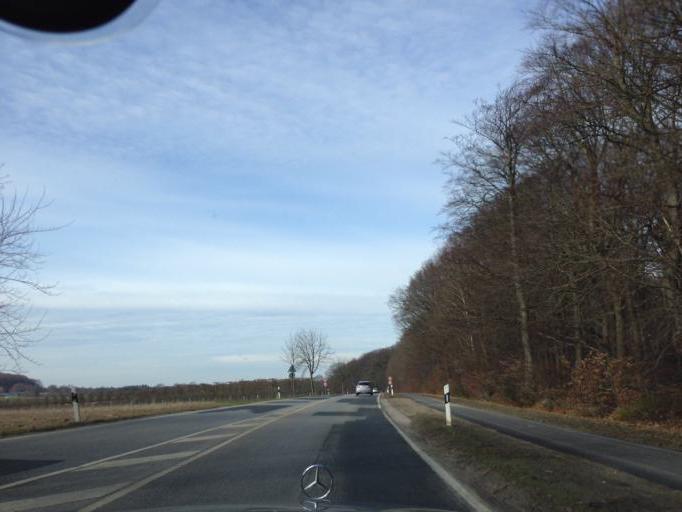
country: DE
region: Lower Saxony
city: Seevetal
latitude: 53.4341
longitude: 9.9195
